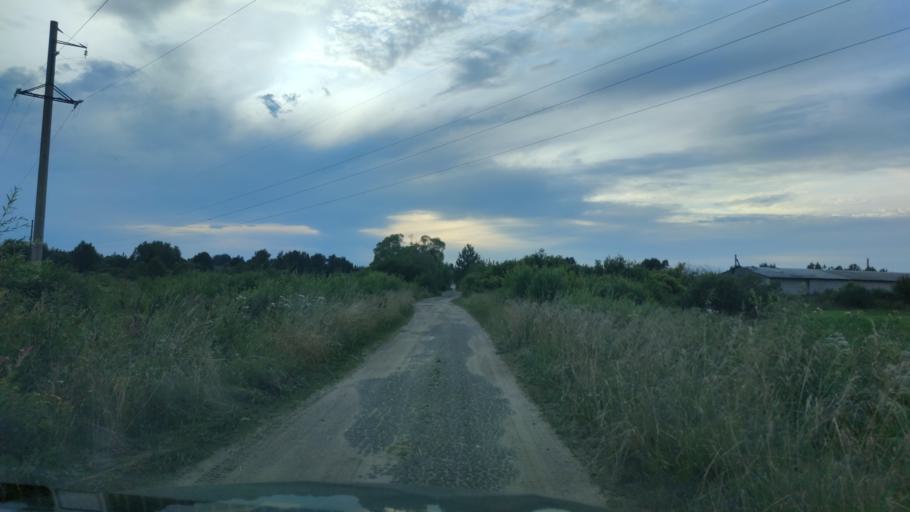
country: BY
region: Vitebsk
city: Mosar
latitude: 55.1267
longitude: 27.1658
